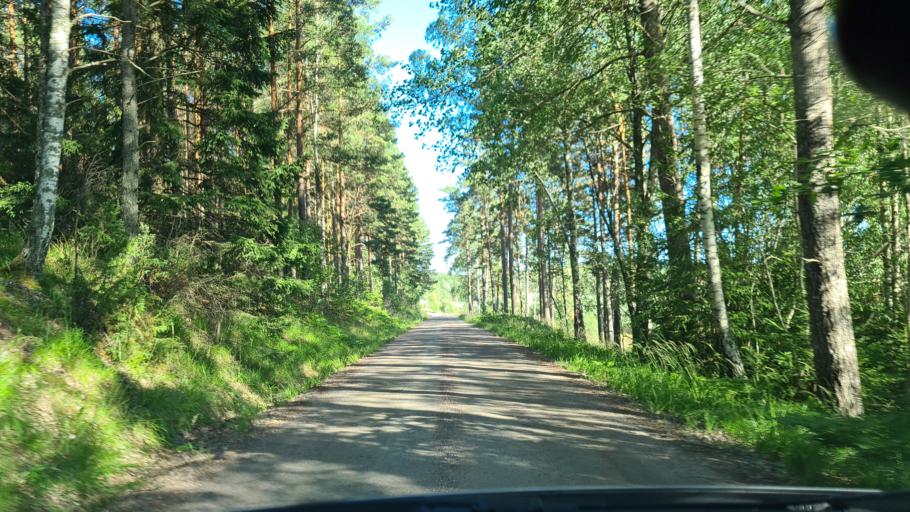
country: SE
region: Soedermanland
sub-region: Nykopings Kommun
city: Stigtomta
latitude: 58.9107
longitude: 16.9222
